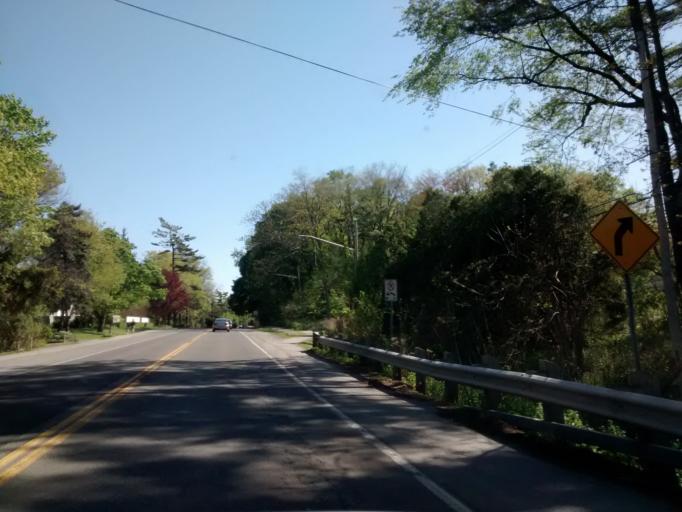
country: CA
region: Ontario
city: Oakville
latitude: 43.4136
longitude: -79.6915
